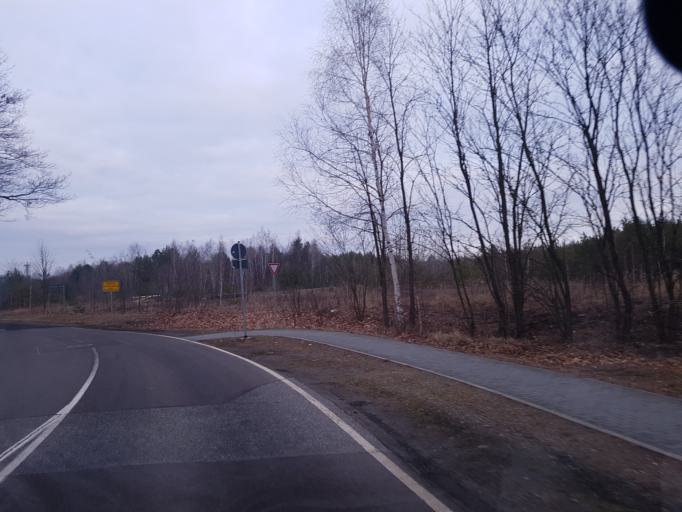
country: DE
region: Brandenburg
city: Senftenberg
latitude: 51.5269
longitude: 13.9624
